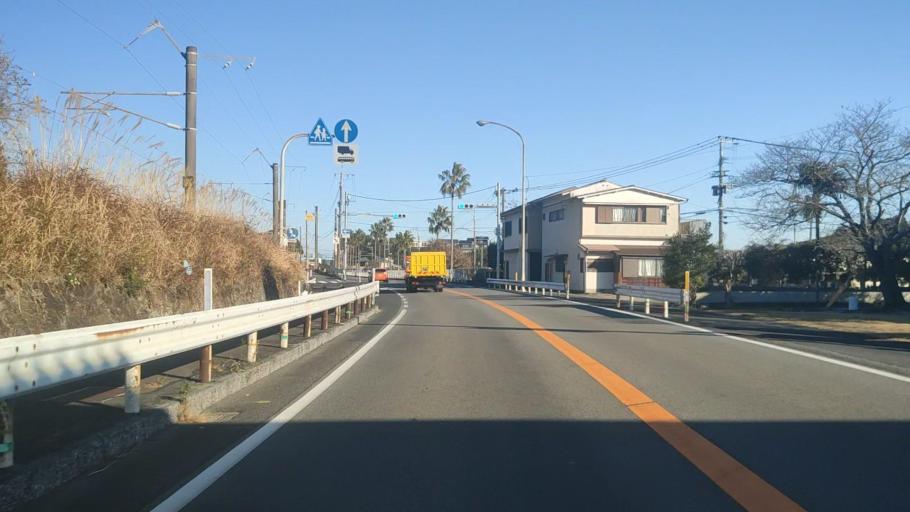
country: JP
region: Miyazaki
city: Nobeoka
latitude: 32.5137
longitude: 131.6823
